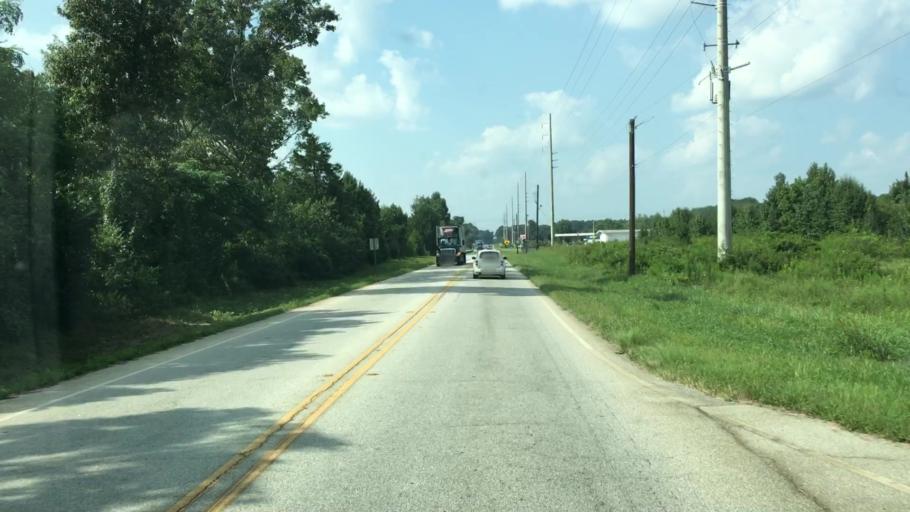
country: US
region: Georgia
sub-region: Walton County
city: Social Circle
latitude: 33.5960
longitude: -83.7495
